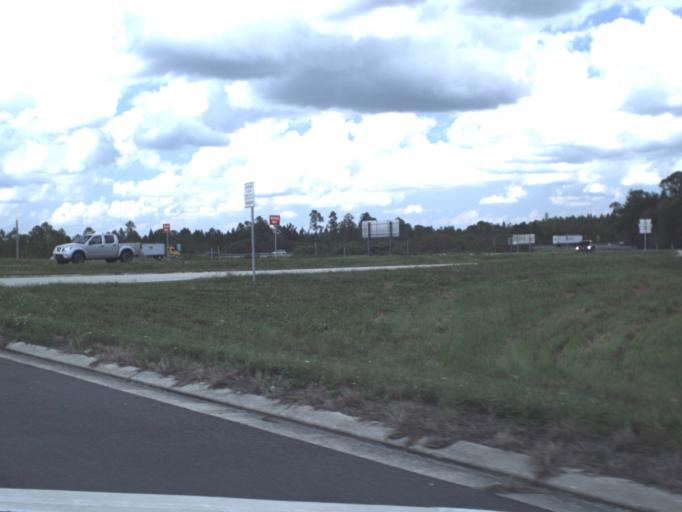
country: US
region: Florida
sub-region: Polk County
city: Polk City
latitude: 28.1801
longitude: -81.7428
